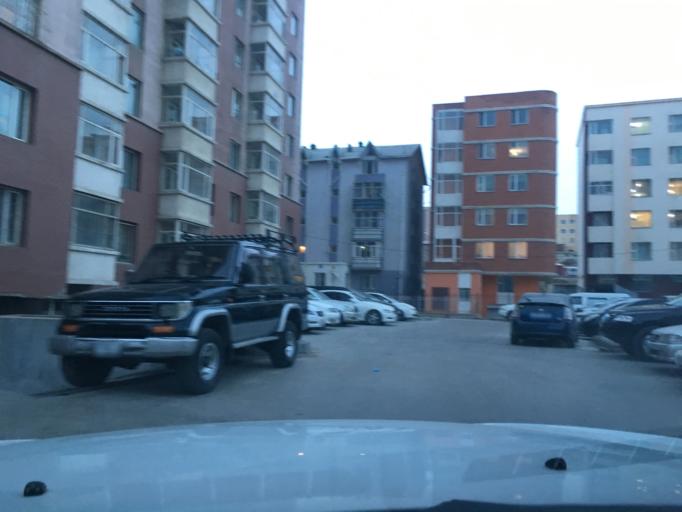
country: MN
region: Ulaanbaatar
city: Ulaanbaatar
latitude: 47.9169
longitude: 106.8598
